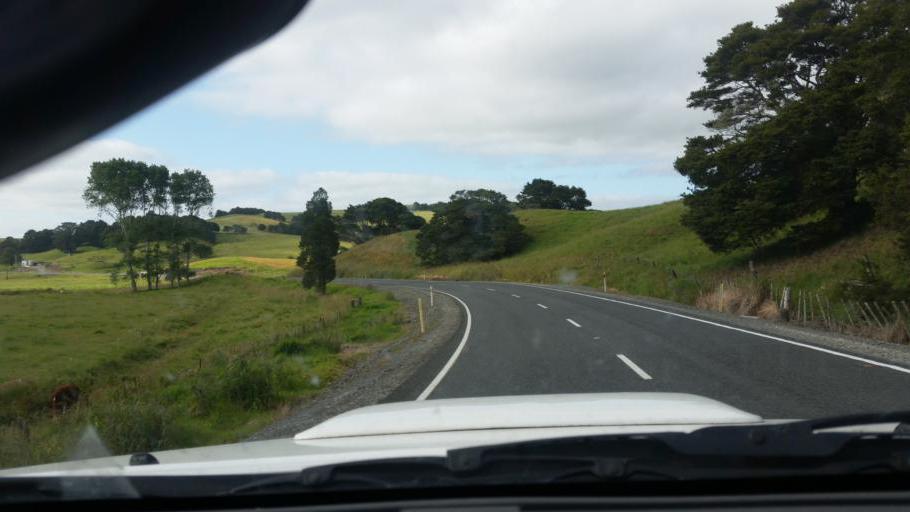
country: NZ
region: Northland
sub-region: Kaipara District
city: Dargaville
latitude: -35.8460
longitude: 173.8436
